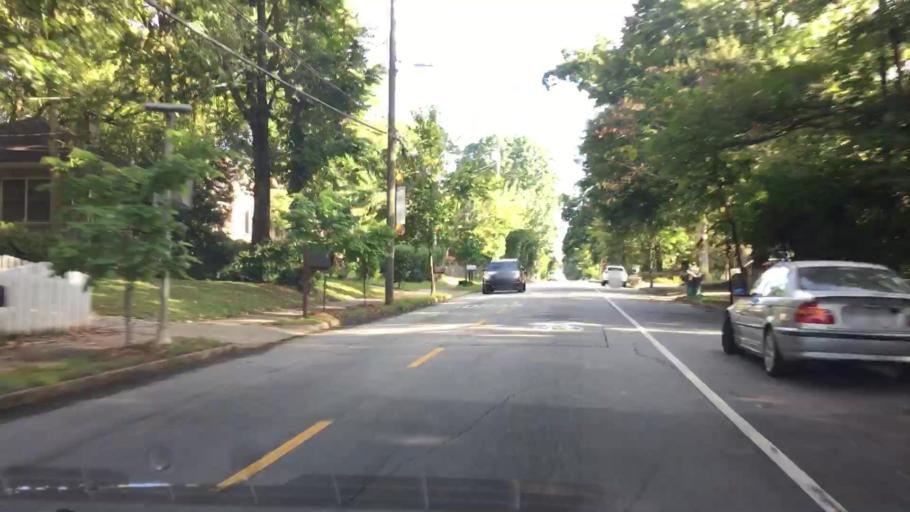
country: US
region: Georgia
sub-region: DeKalb County
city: Druid Hills
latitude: 33.7542
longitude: -84.3421
